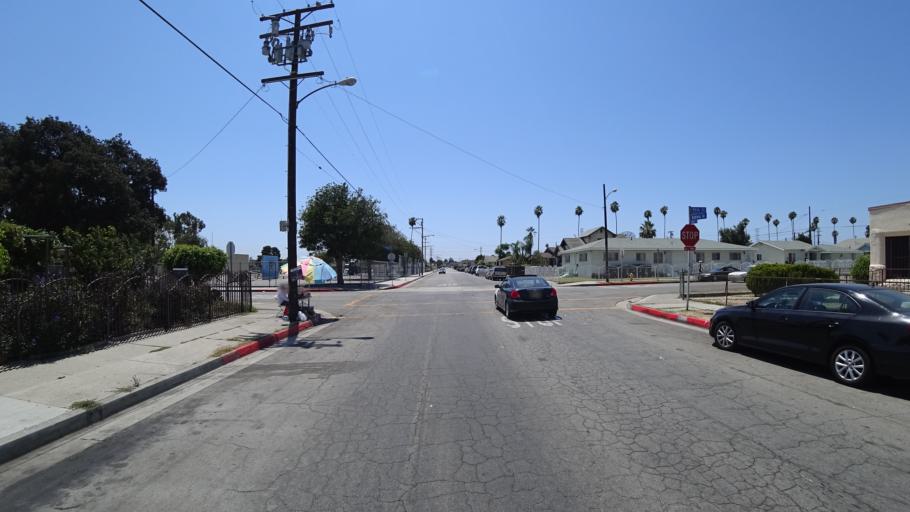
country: US
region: California
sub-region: Los Angeles County
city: Westmont
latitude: 33.9499
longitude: -118.2959
